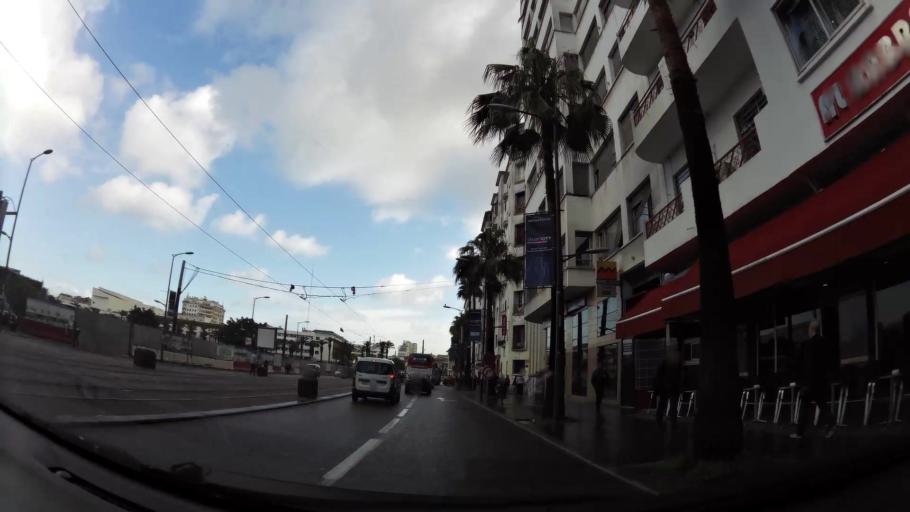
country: MA
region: Grand Casablanca
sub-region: Casablanca
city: Casablanca
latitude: 33.5886
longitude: -7.6206
